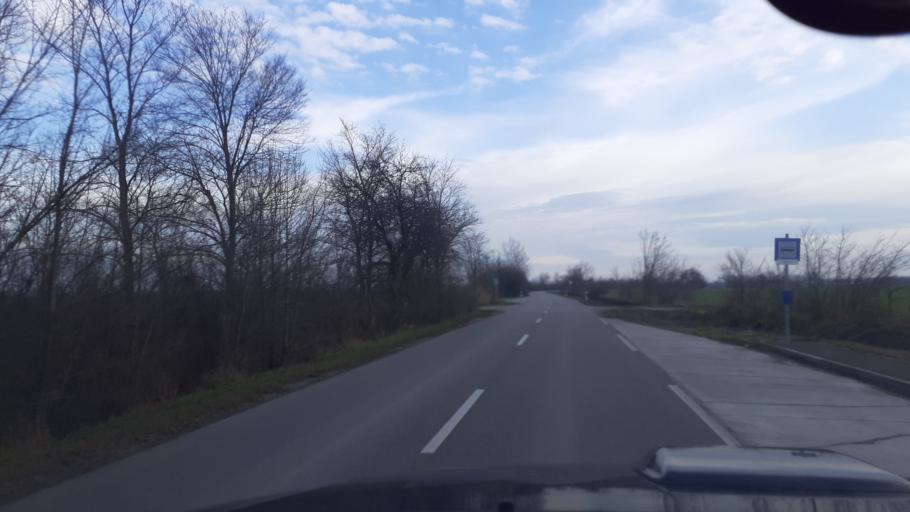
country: HU
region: Bacs-Kiskun
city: Szabadszallas
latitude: 46.9185
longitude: 19.1879
